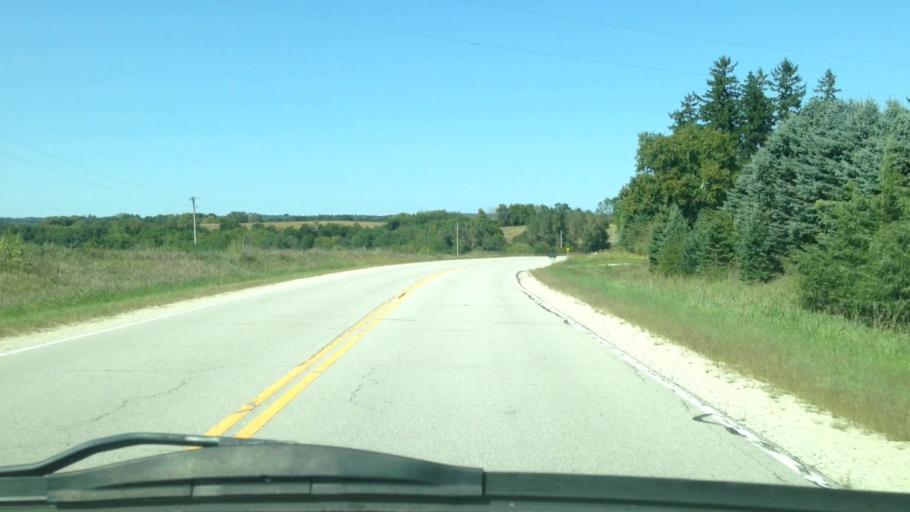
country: US
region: Minnesota
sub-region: Fillmore County
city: Rushford
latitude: 43.6404
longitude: -91.7903
